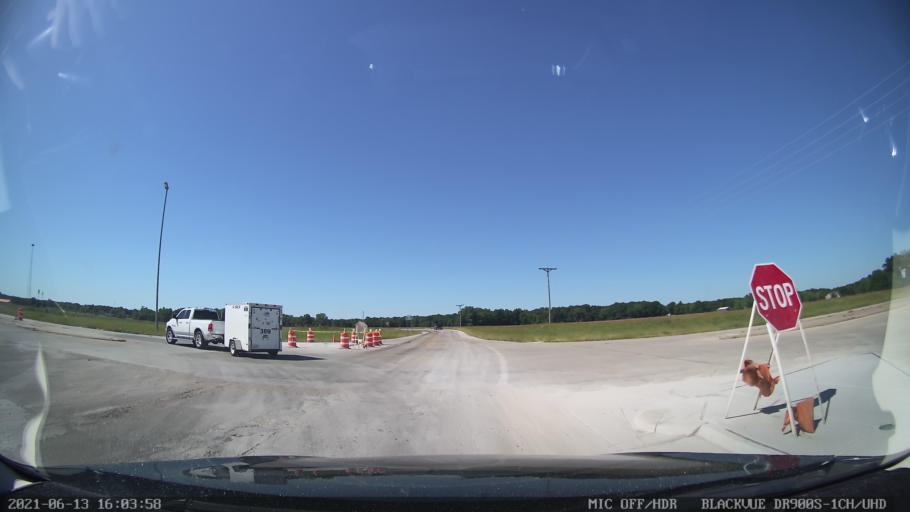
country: US
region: Illinois
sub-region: Montgomery County
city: Raymond
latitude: 39.2777
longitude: -89.6364
